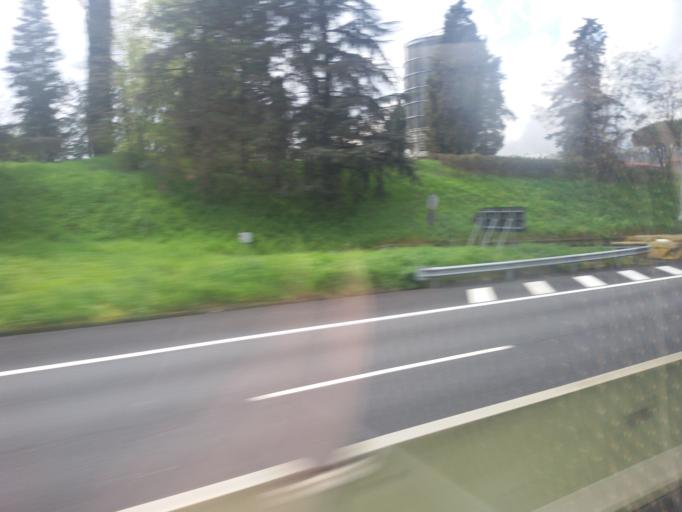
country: IT
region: Tuscany
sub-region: Province of Florence
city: Incisa in Val d'Arno
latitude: 43.6644
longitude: 11.4596
